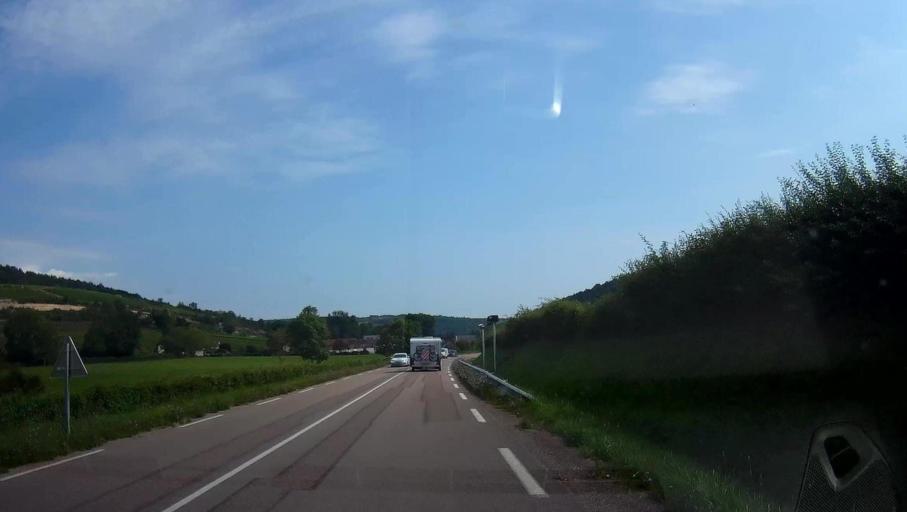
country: FR
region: Bourgogne
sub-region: Departement de la Cote-d'Or
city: Meursault
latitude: 46.9783
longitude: 4.7053
